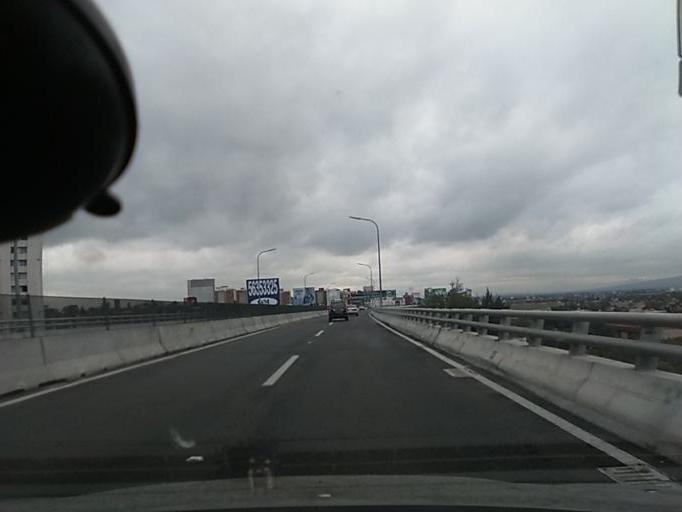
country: MX
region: Mexico City
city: Tlalpan
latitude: 19.3033
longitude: -99.1819
